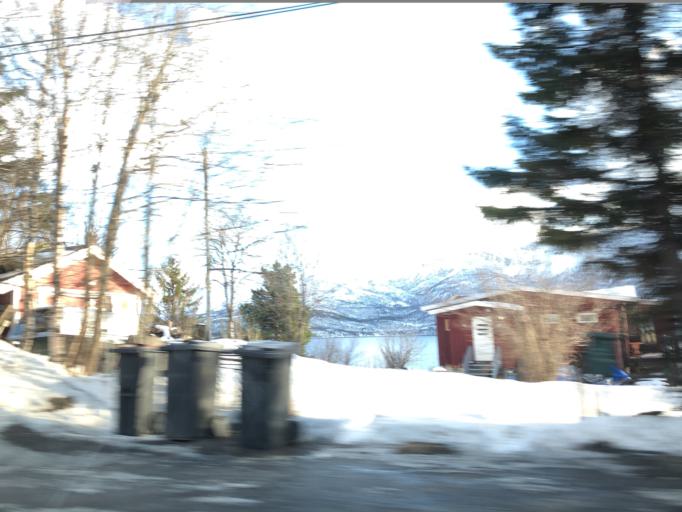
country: NO
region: Nordland
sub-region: Narvik
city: Bjerkvik
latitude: 68.4642
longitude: 17.6754
